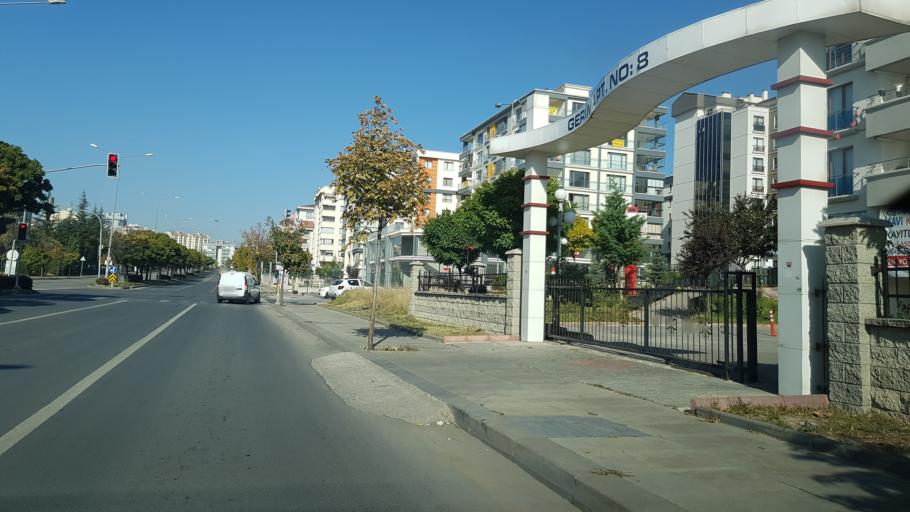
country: TR
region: Ankara
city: Etimesgut
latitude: 39.9725
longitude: 32.6086
